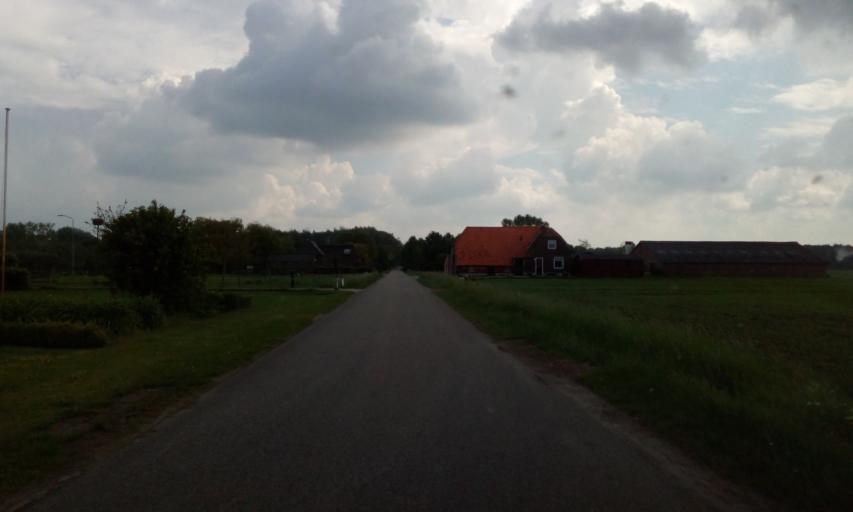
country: NL
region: Gelderland
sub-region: Gemeente Voorst
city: Voorst
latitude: 52.1680
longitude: 6.0956
